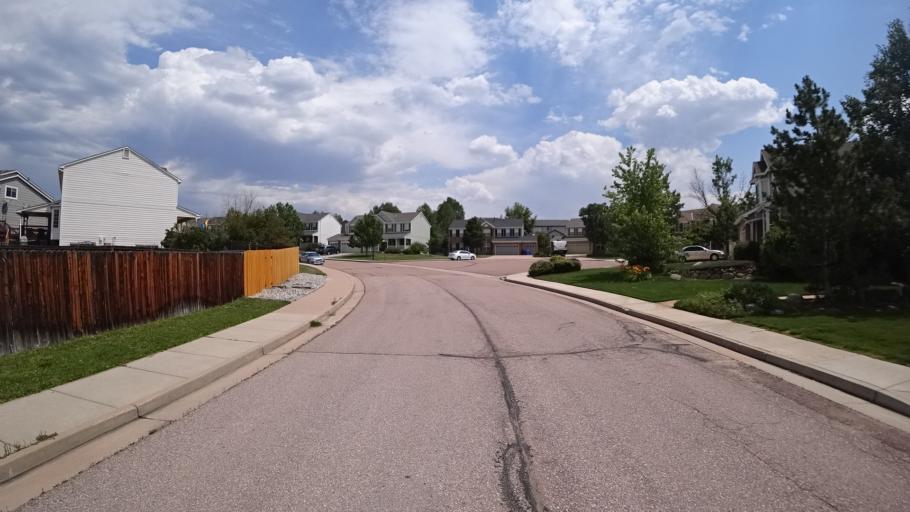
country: US
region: Colorado
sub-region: El Paso County
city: Black Forest
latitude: 38.9616
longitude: -104.7432
